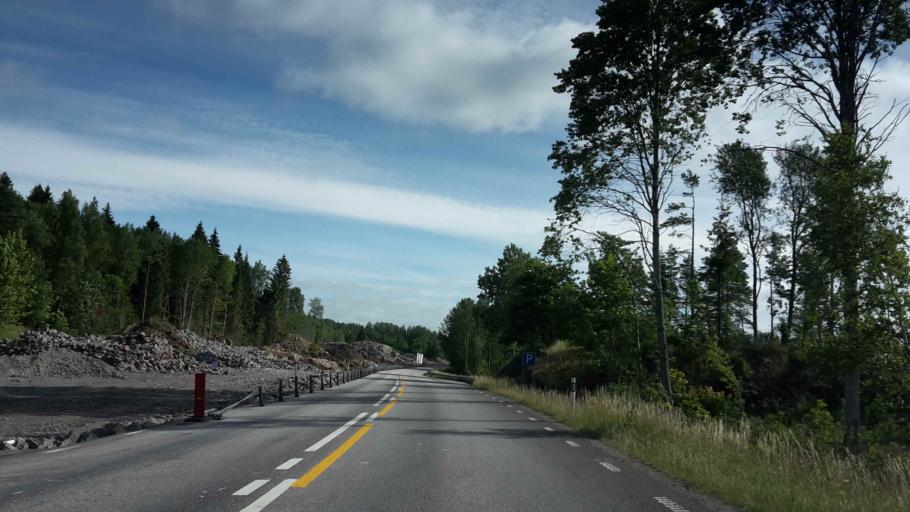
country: SE
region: OErebro
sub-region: Askersunds Kommun
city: Askersund
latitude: 58.8961
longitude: 14.9372
